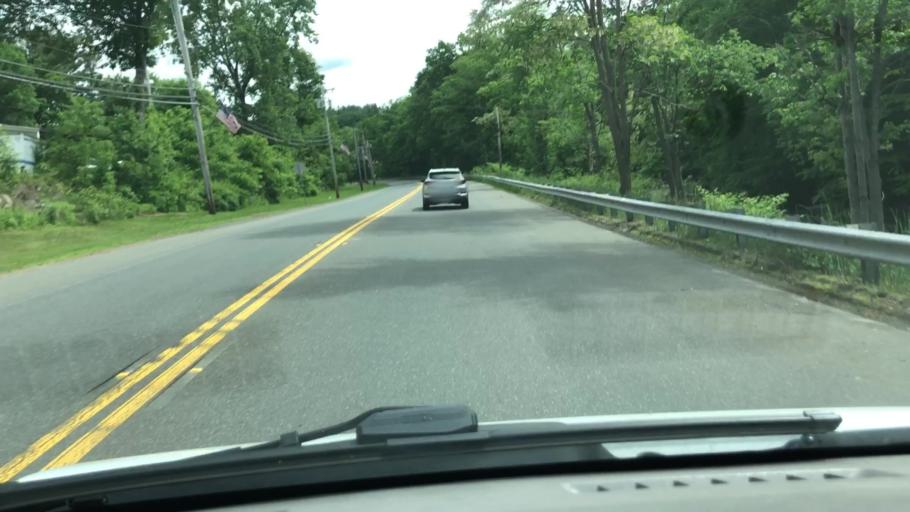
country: US
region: Massachusetts
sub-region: Hampshire County
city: Williamsburg
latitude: 42.3864
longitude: -72.7171
